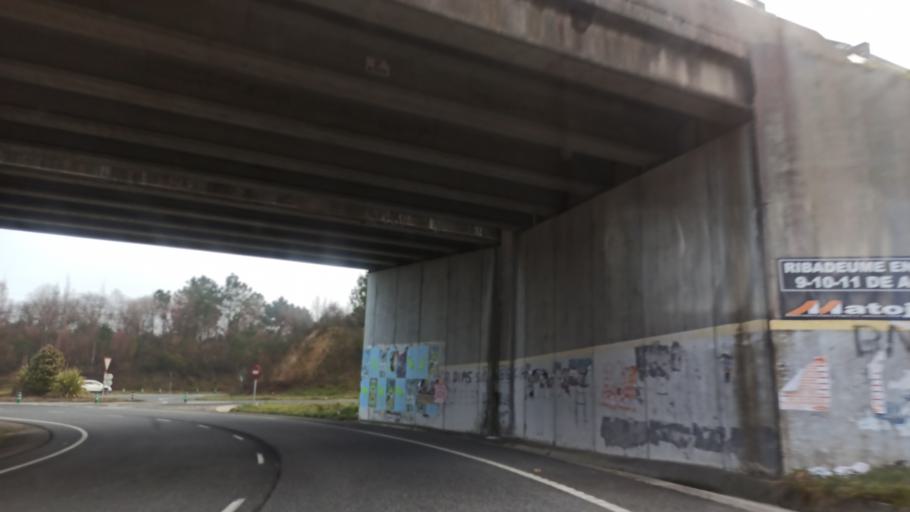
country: ES
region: Galicia
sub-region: Provincia da Coruna
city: As Pontes de Garcia Rodriguez
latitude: 43.4401
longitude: -7.8833
